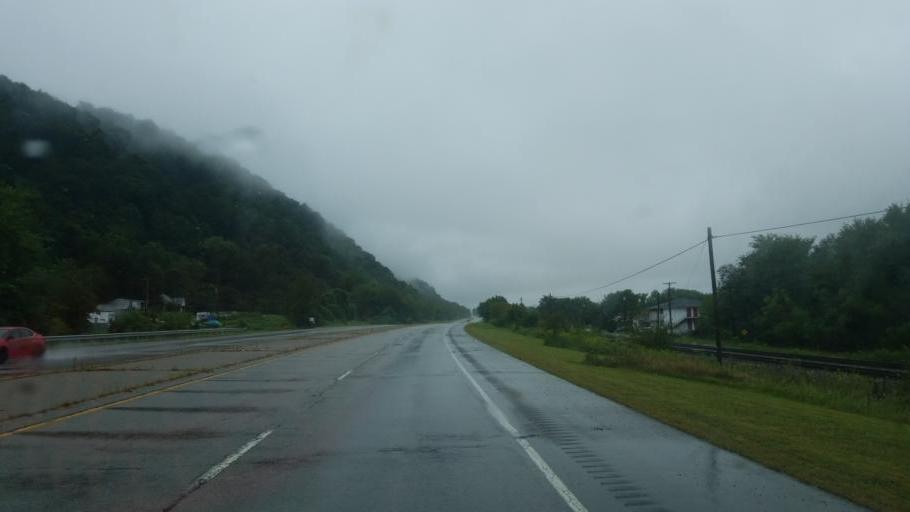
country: US
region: Kentucky
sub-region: Greenup County
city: South Shore
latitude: 38.7205
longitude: -82.9727
